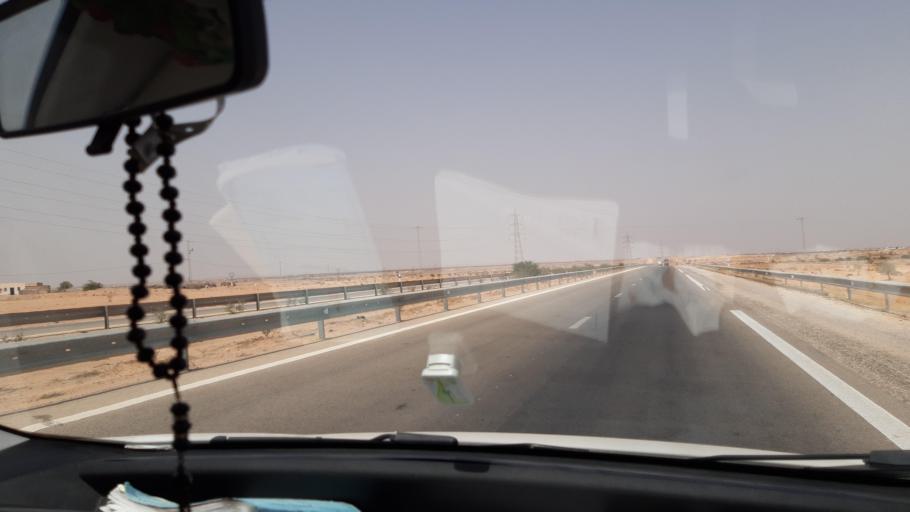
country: TN
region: Safaqis
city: Skhira
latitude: 34.1657
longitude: 9.9721
